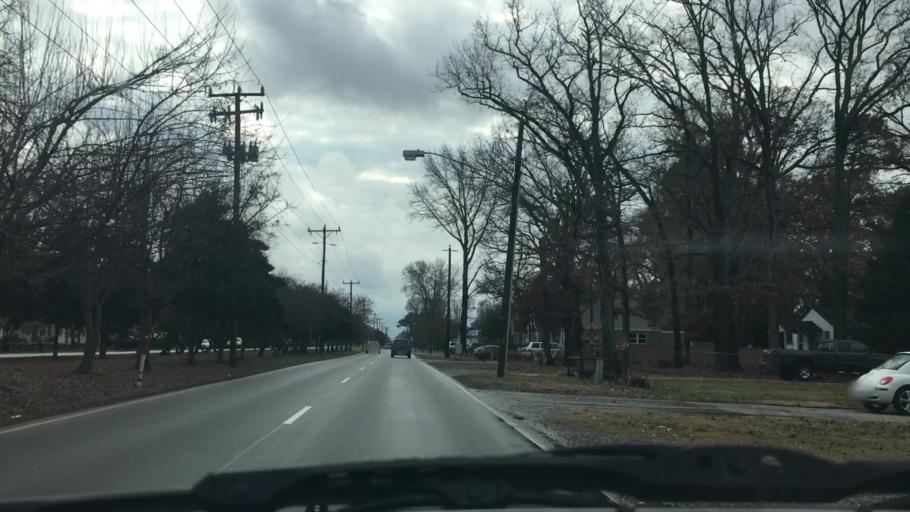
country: US
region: Virginia
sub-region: City of Norfolk
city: Norfolk
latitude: 36.9219
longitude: -76.2428
